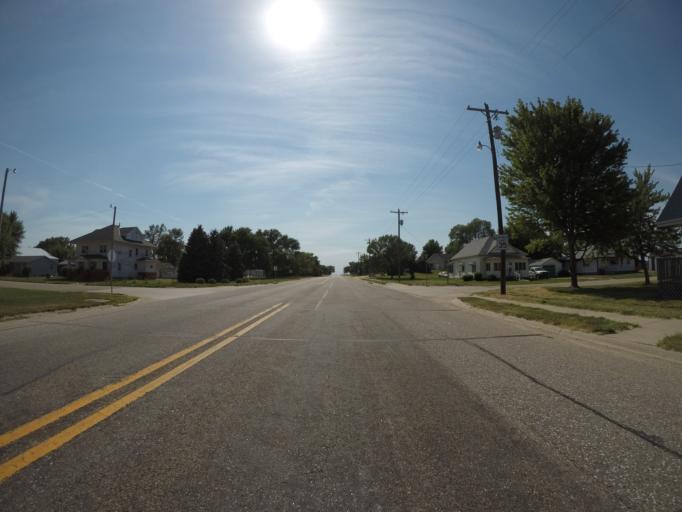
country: US
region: Nebraska
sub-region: Adams County
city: Hastings
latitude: 40.4663
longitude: -98.6518
